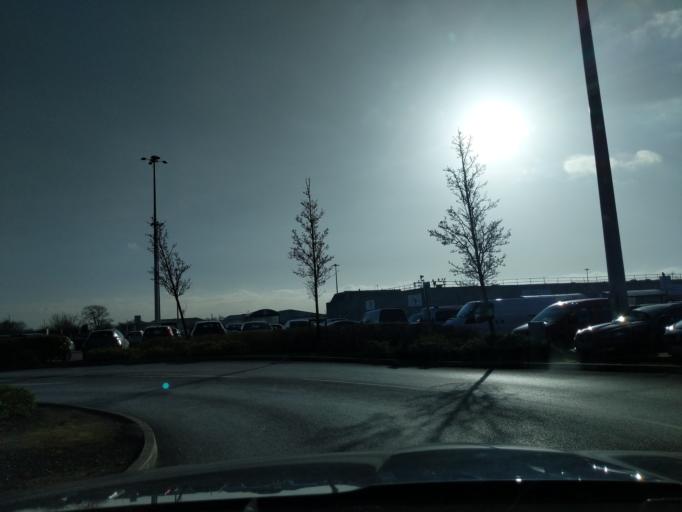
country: GB
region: England
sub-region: Sunderland
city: Washington
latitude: 54.9020
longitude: -1.5310
